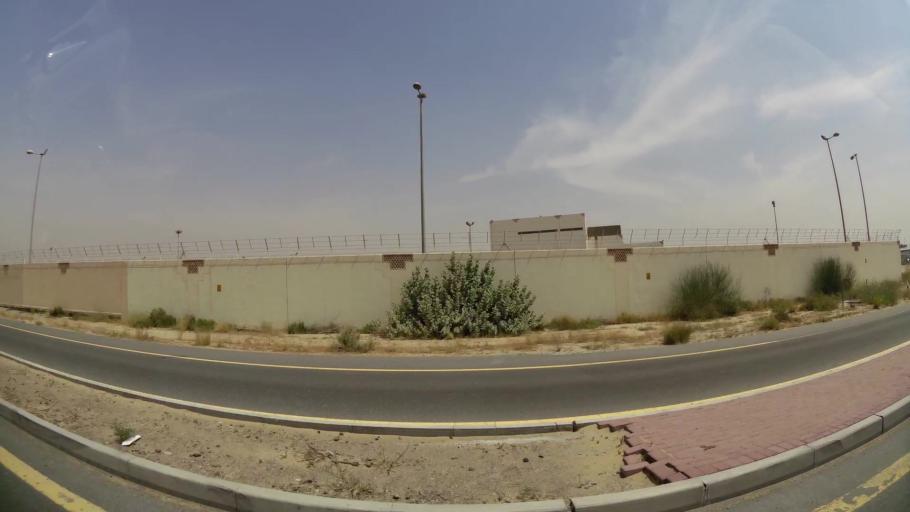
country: AE
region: Ash Shariqah
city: Sharjah
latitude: 25.2343
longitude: 55.4076
